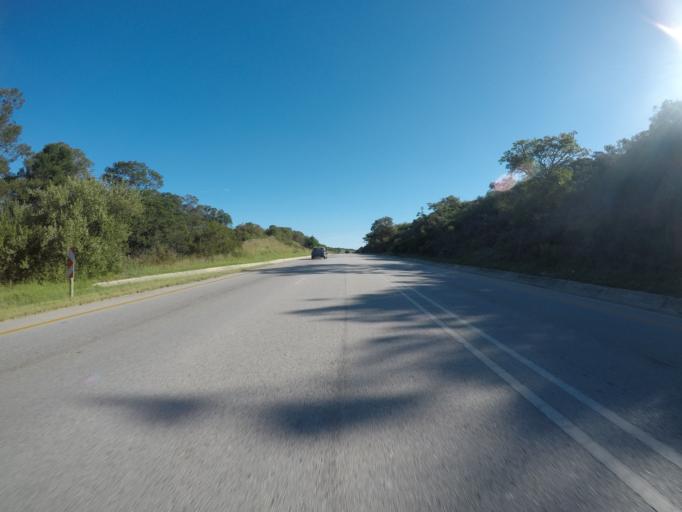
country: ZA
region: Eastern Cape
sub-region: Cacadu District Municipality
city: Jeffrey's Bay
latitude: -33.9076
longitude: 25.0740
